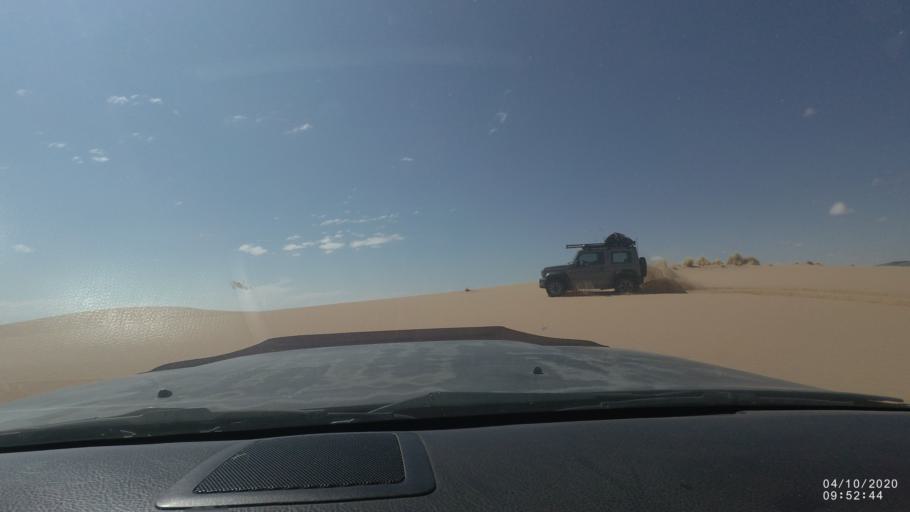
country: BO
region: Oruro
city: Poopo
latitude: -18.7070
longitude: -67.4976
